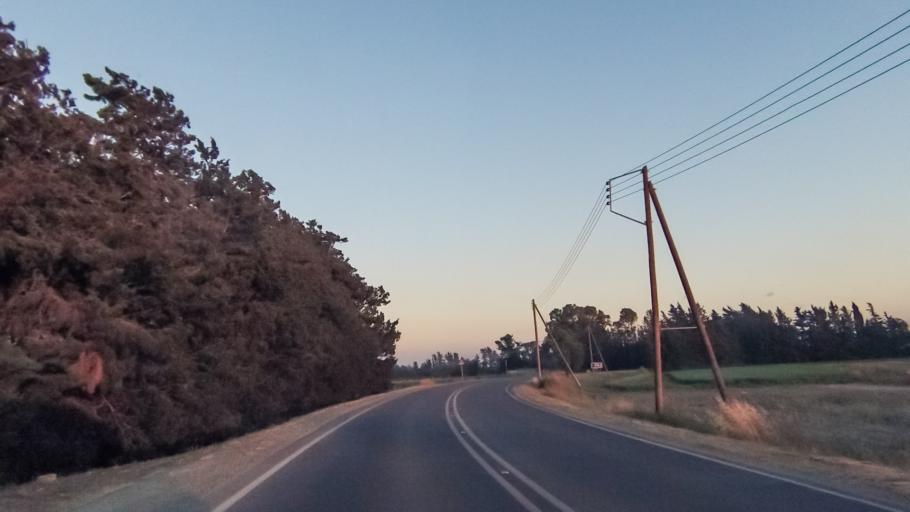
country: CY
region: Larnaka
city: Kolossi
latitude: 34.6539
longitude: 32.9418
